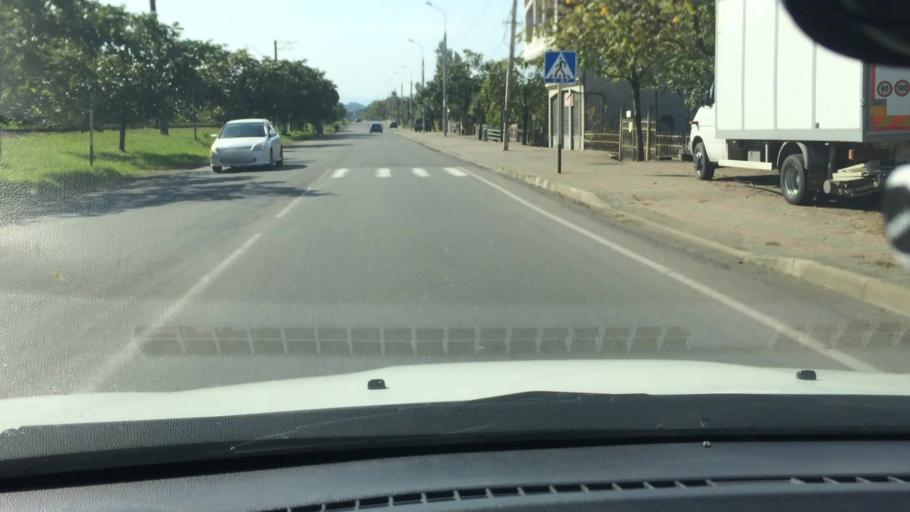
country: GE
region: Ajaria
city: Kobuleti
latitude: 41.8014
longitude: 41.7749
